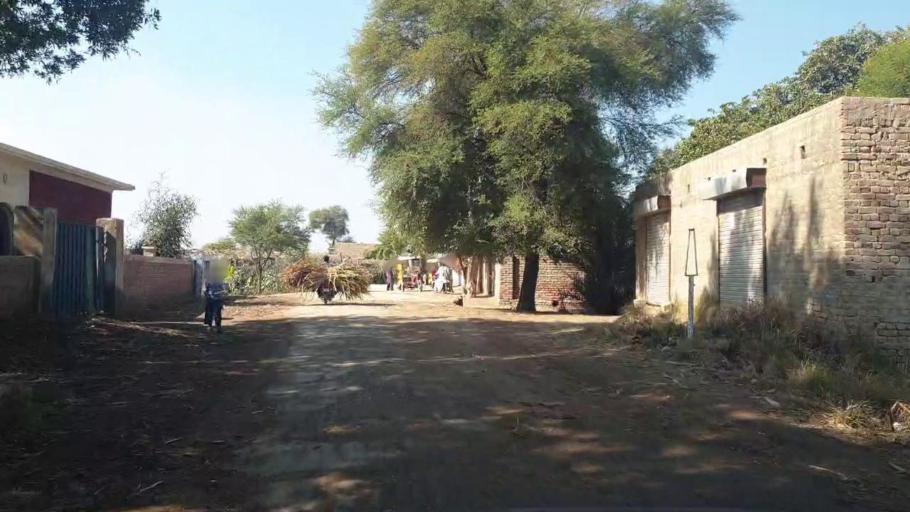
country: PK
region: Sindh
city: Shahdadpur
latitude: 25.9140
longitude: 68.5869
